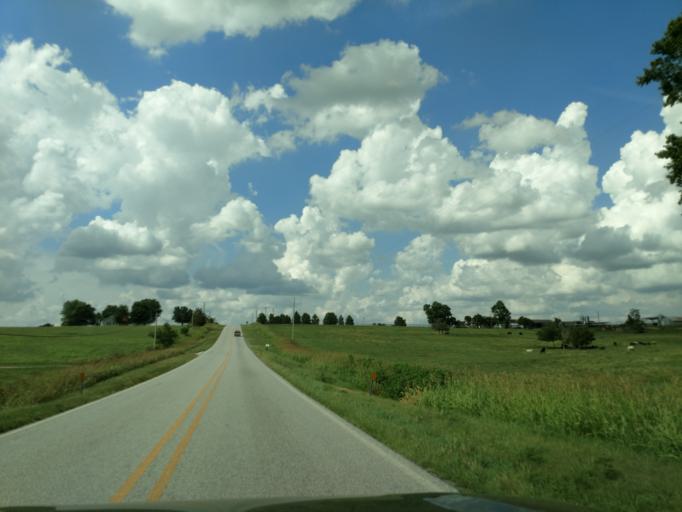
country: US
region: Arkansas
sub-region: Carroll County
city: Berryville
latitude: 36.4327
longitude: -93.5563
